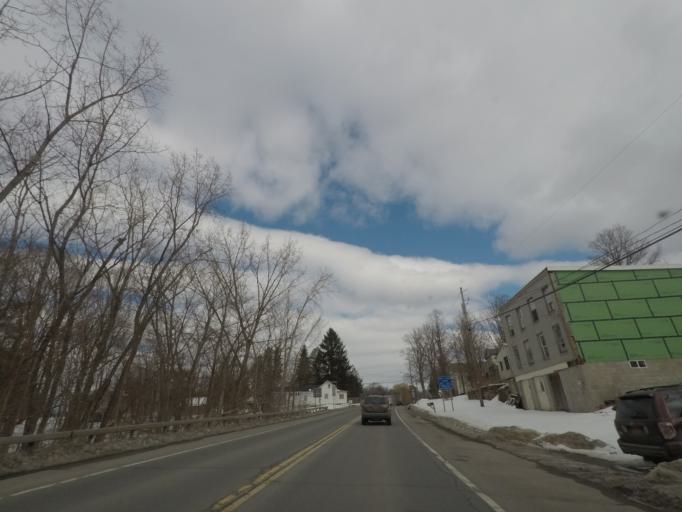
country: US
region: New York
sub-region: Washington County
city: Greenwich
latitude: 43.0996
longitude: -73.5249
